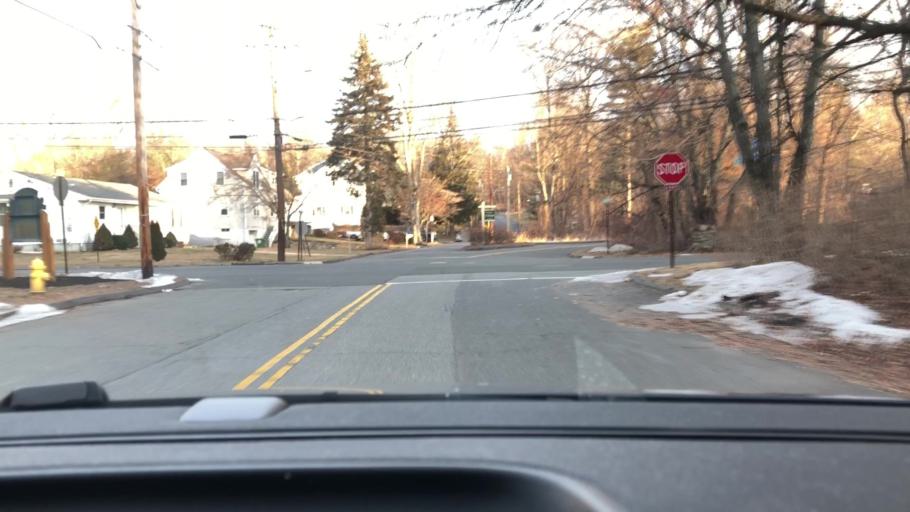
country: US
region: Connecticut
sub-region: Fairfield County
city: Trumbull
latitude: 41.2280
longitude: -73.2122
